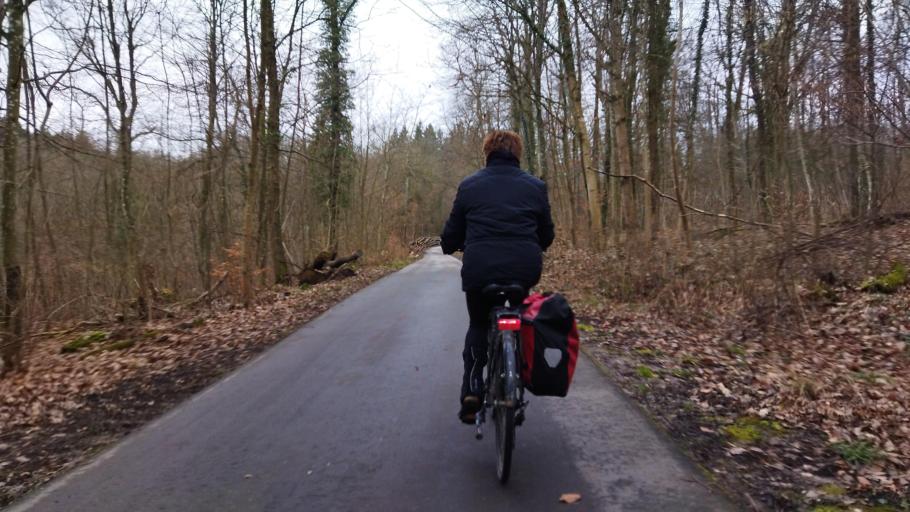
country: DE
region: Baden-Wuerttemberg
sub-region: Regierungsbezirk Stuttgart
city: Heilbronn
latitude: 49.1219
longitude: 9.2459
